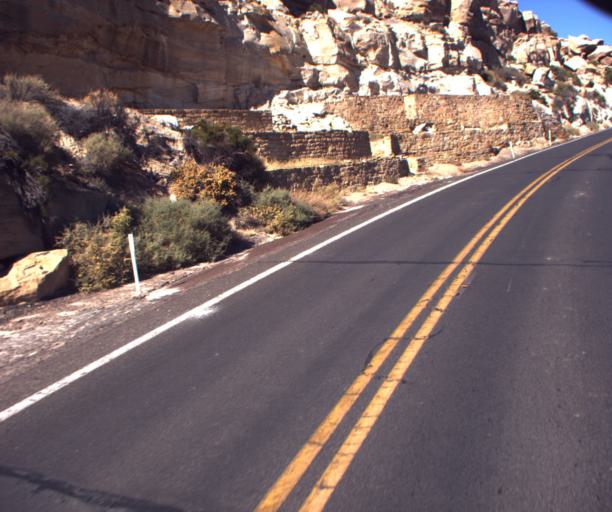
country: US
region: Arizona
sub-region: Navajo County
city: First Mesa
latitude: 35.8109
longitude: -110.5286
